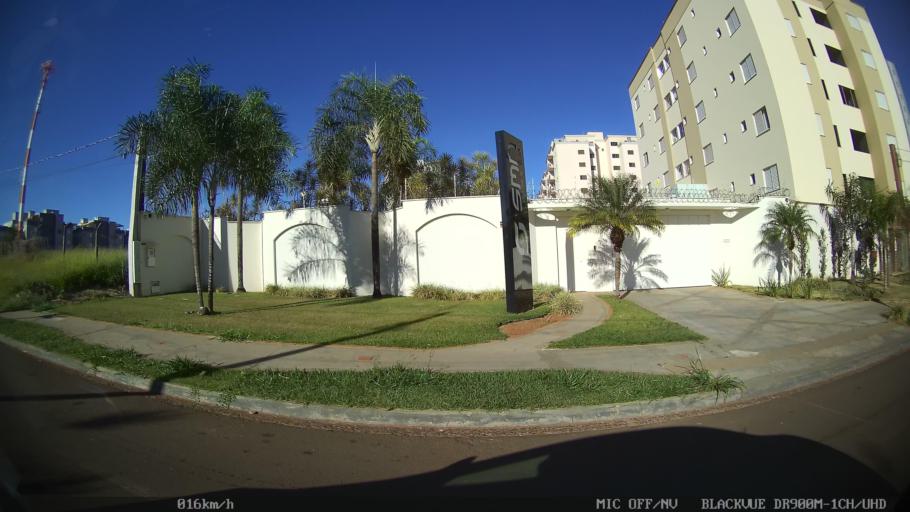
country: BR
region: Sao Paulo
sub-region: Franca
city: Franca
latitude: -20.5628
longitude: -47.4039
